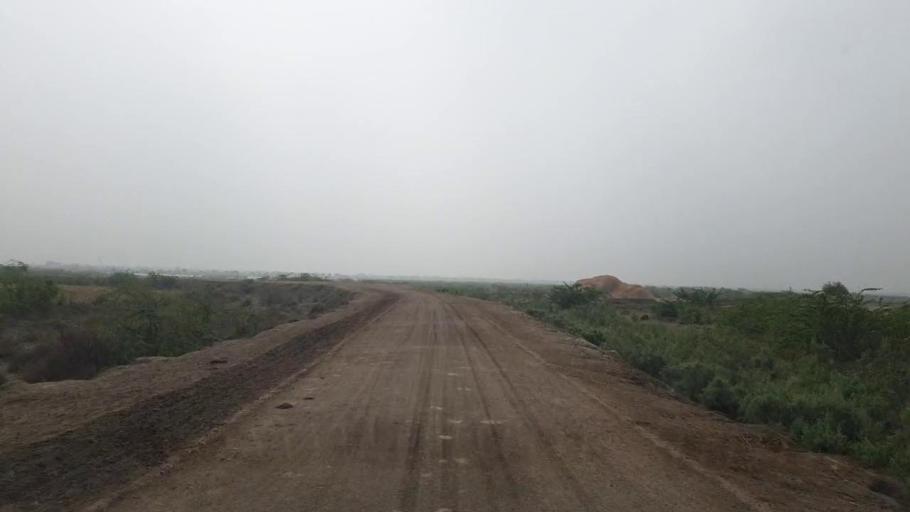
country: PK
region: Sindh
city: Badin
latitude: 24.5820
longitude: 68.6806
